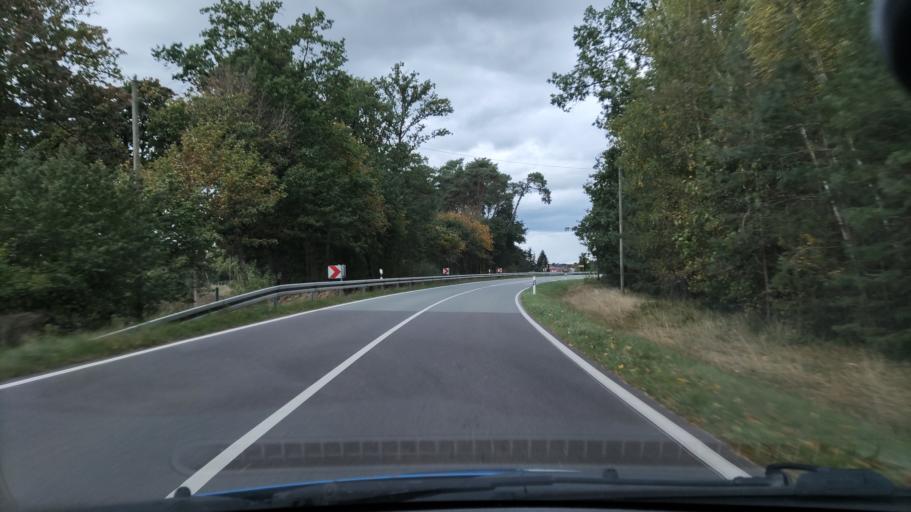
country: DE
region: Mecklenburg-Vorpommern
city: Lubtheen
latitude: 53.3549
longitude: 10.9581
